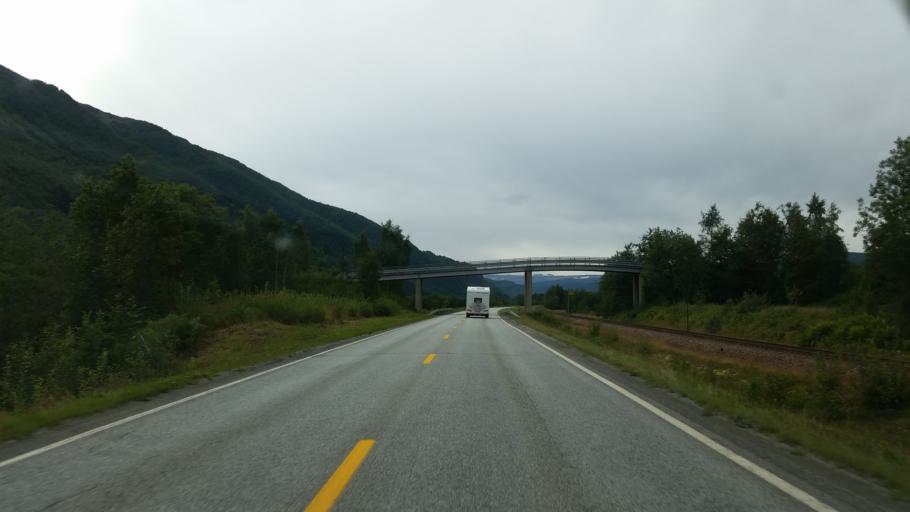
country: NO
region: Nordland
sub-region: Saltdal
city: Rognan
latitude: 67.0465
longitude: 15.3832
